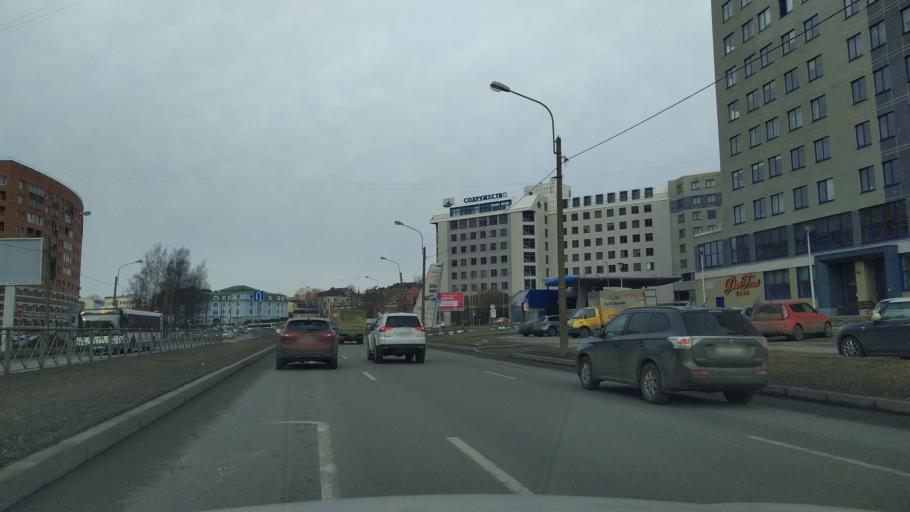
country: RU
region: St.-Petersburg
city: Kolomyagi
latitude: 60.0131
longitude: 30.2945
